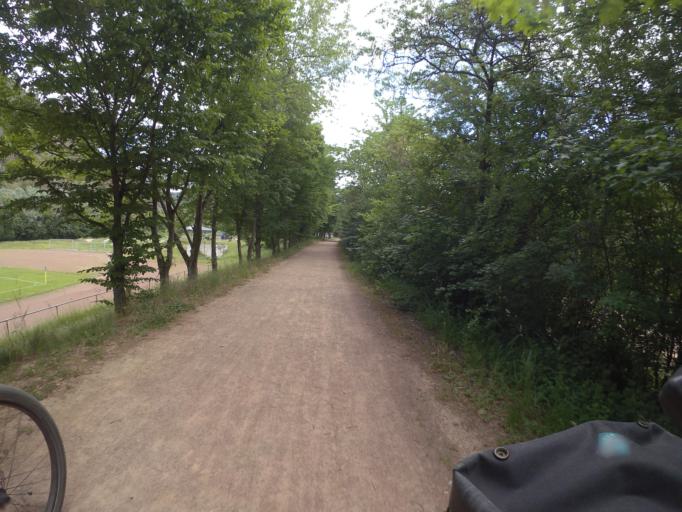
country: DE
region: Rheinland-Pfalz
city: Bad Munster am Stein-Ebernburg
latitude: 49.8144
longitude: 7.8315
